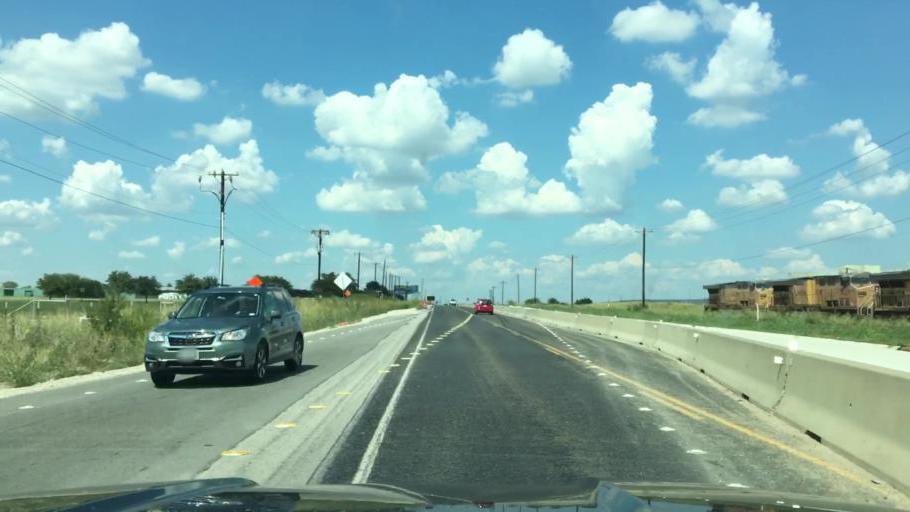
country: US
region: Texas
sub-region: Denton County
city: Justin
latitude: 33.0340
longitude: -97.3080
